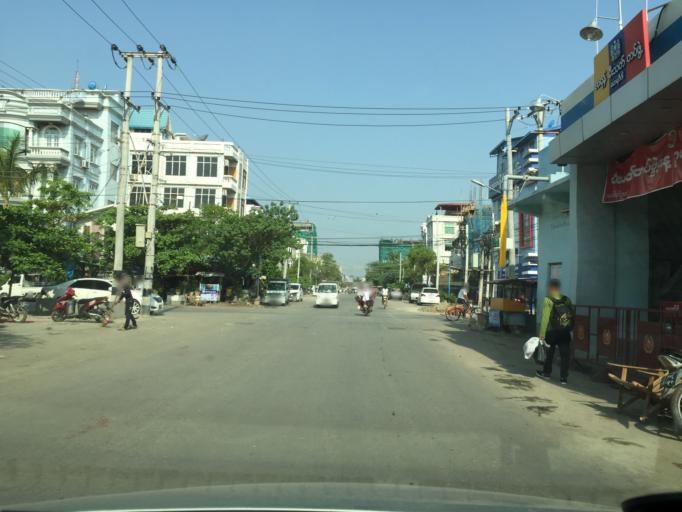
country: MM
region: Mandalay
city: Mandalay
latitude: 21.9735
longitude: 96.0919
